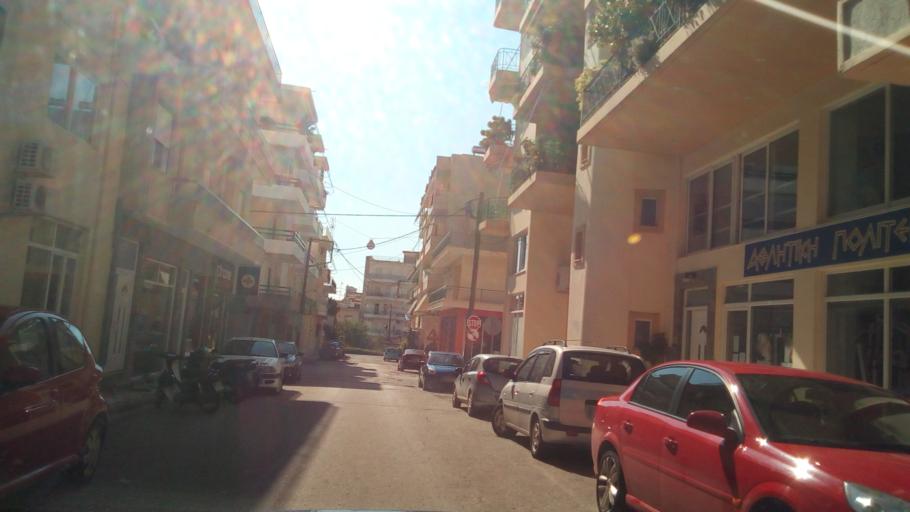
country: GR
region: West Greece
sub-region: Nomos Aitolias kai Akarnanias
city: Nafpaktos
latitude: 38.3935
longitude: 21.8408
